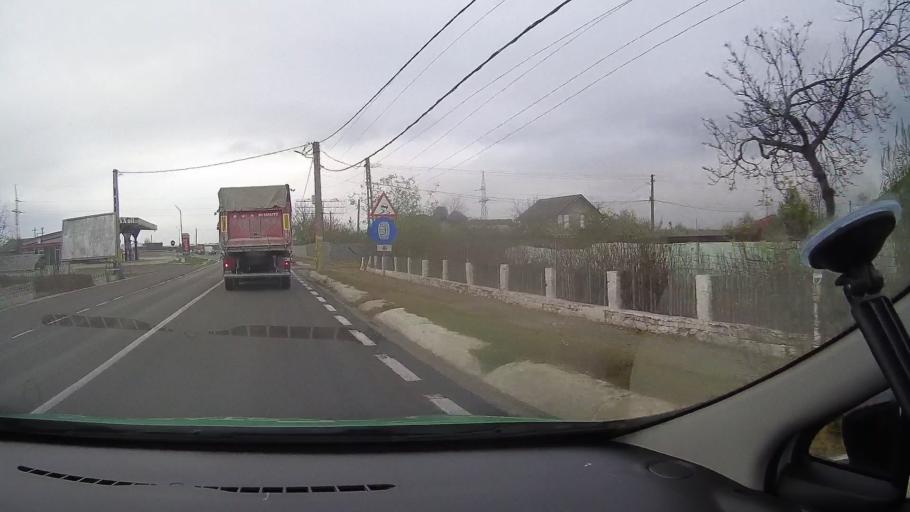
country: RO
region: Constanta
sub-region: Comuna Poarta Alba
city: Poarta Alba
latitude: 44.2115
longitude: 28.3946
